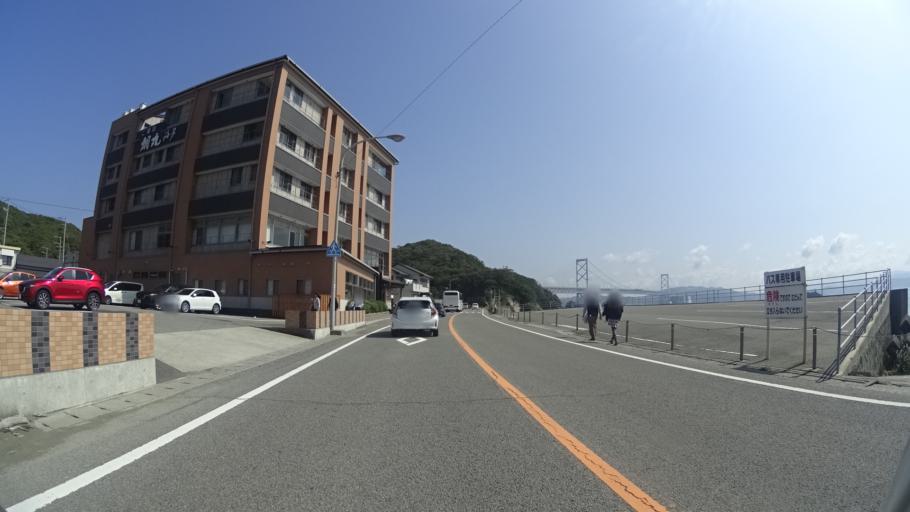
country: JP
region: Tokushima
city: Narutocho-mitsuishi
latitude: 34.2285
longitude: 134.6364
